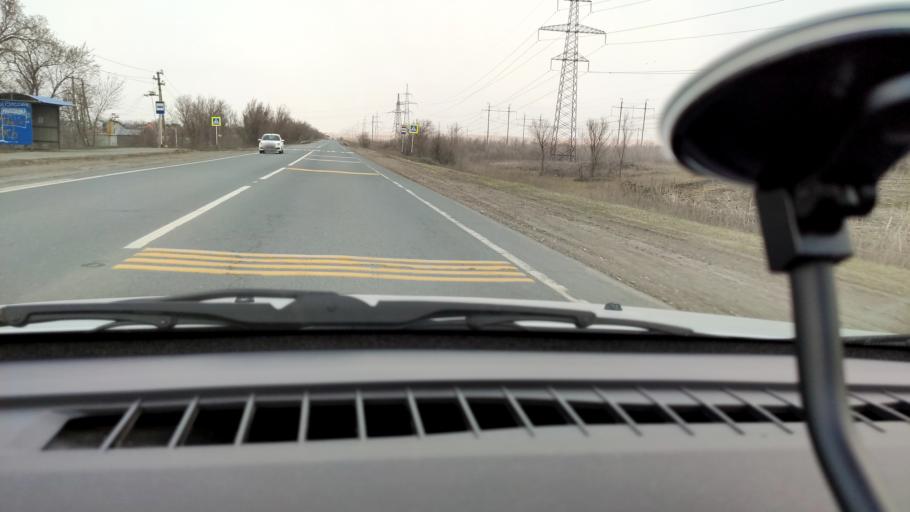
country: RU
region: Samara
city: Dubovyy Umet
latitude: 53.0820
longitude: 50.3908
